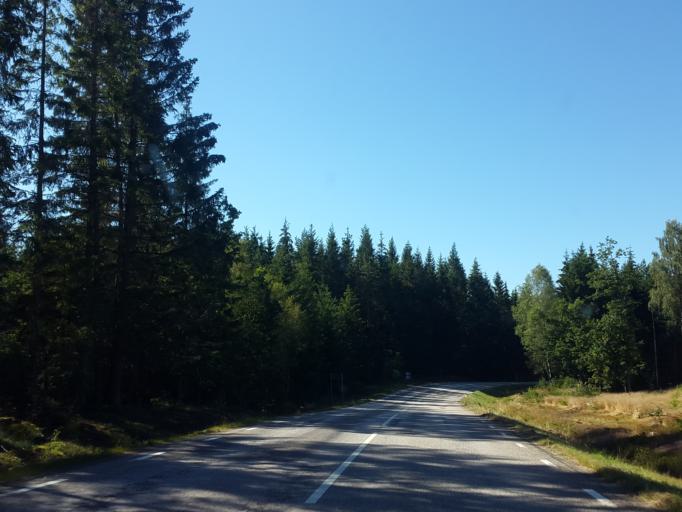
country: SE
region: Vaestra Goetaland
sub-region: Herrljunga Kommun
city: Herrljunga
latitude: 57.9851
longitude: 13.0109
